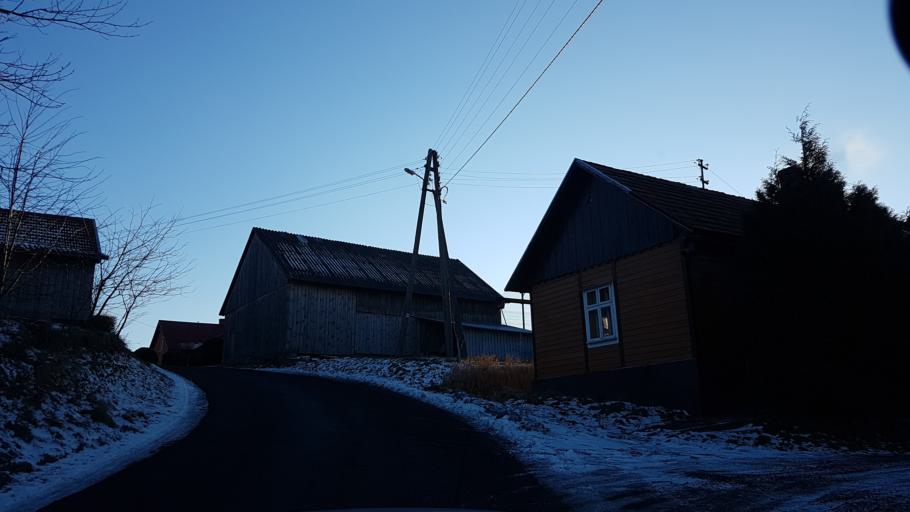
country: PL
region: Lesser Poland Voivodeship
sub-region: Powiat nowosadecki
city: Rytro
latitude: 49.5135
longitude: 20.6685
